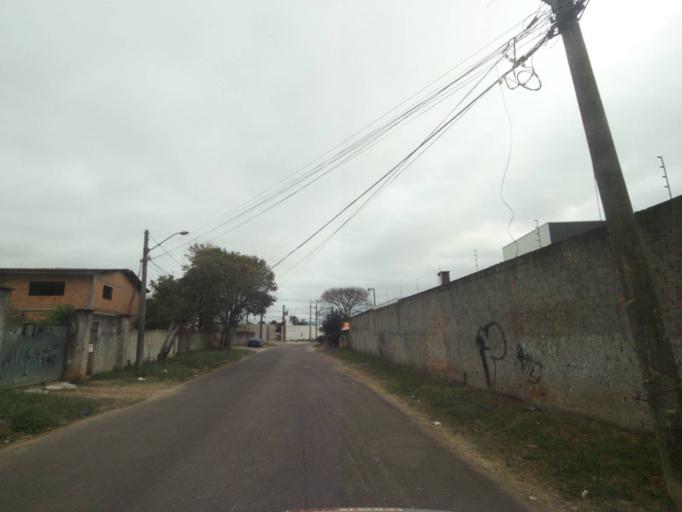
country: BR
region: Parana
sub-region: Sao Jose Dos Pinhais
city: Sao Jose dos Pinhais
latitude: -25.4996
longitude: -49.2140
